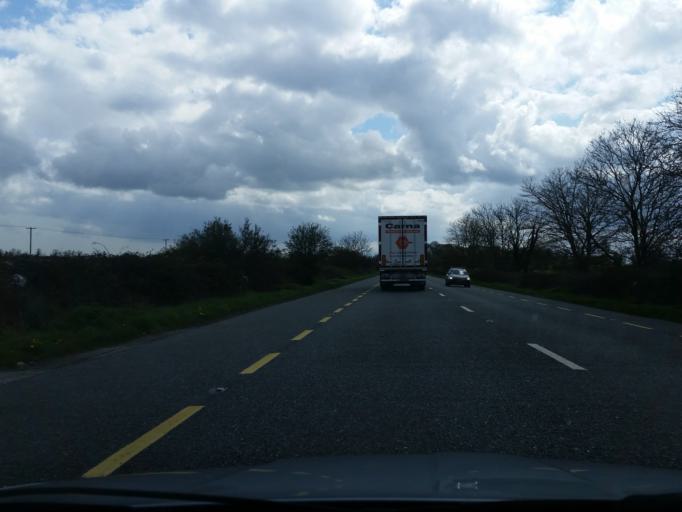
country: IE
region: Leinster
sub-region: An Mhi
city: Ashbourne
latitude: 53.5387
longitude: -6.4258
